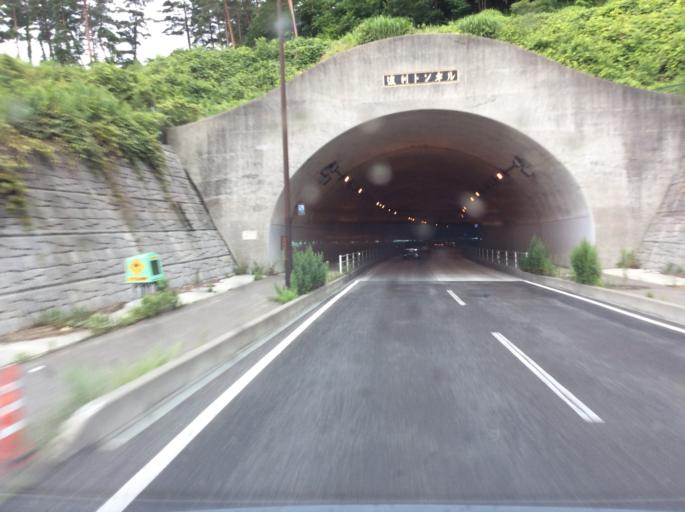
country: JP
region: Fukushima
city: Fukushima-shi
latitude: 37.7334
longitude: 140.4782
